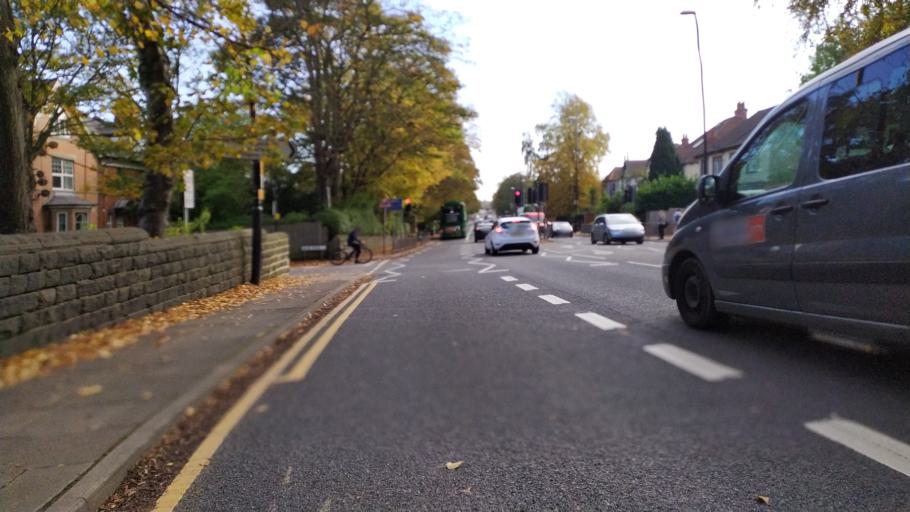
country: GB
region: England
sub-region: City and Borough of Leeds
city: Chapel Allerton
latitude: 53.8306
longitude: -1.5864
